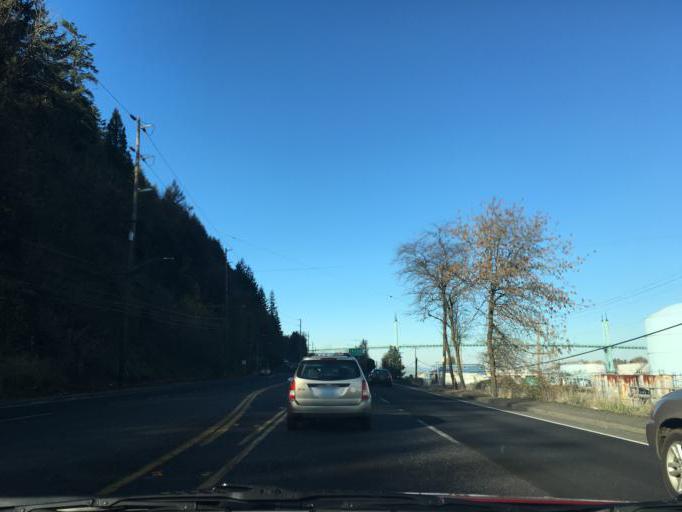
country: US
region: Oregon
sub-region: Washington County
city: West Haven
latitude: 45.5759
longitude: -122.7602
